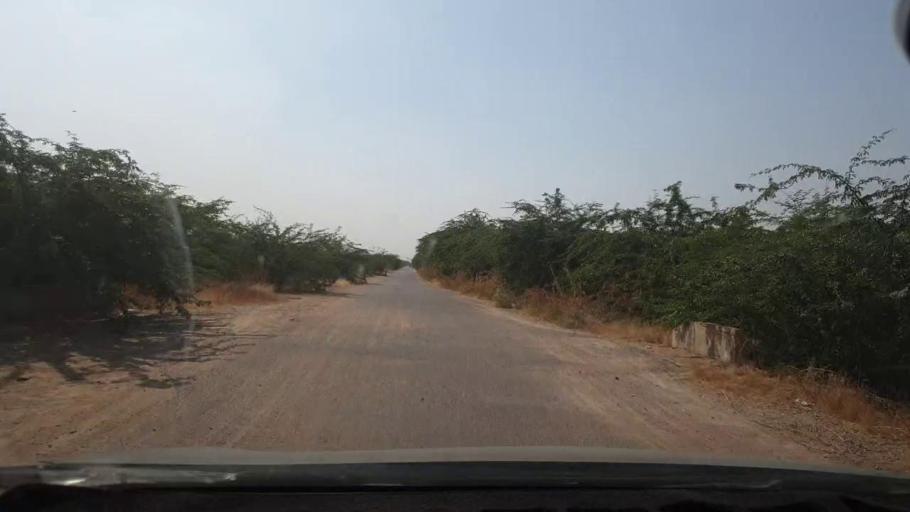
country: PK
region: Sindh
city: Malir Cantonment
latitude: 25.1199
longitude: 67.2159
